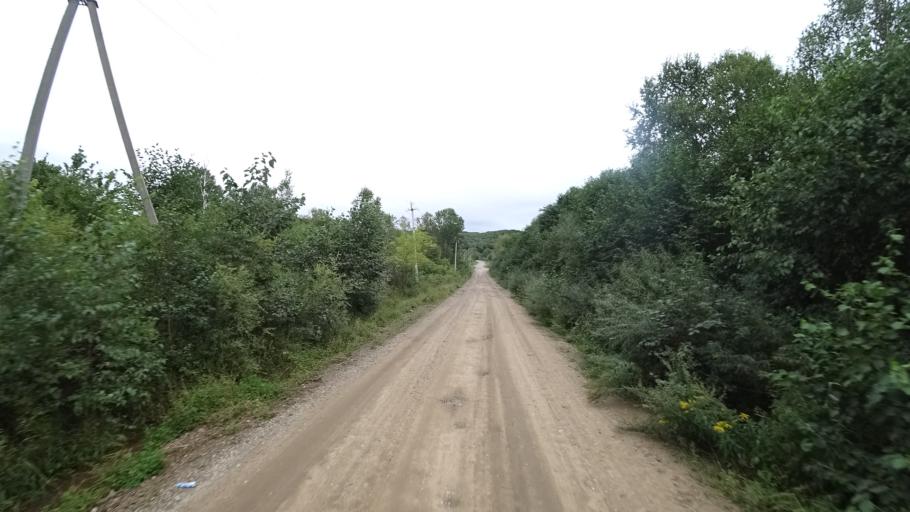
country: RU
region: Primorskiy
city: Rettikhovka
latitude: 44.1694
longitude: 132.7844
